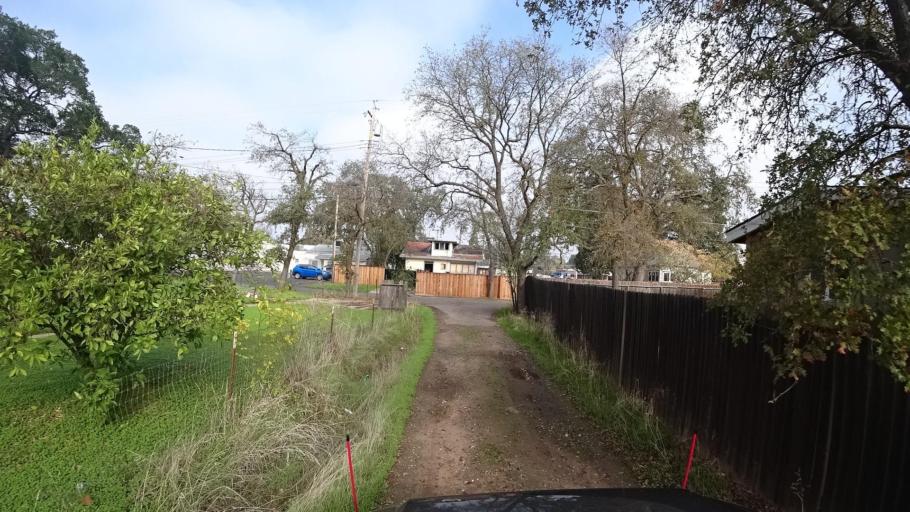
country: US
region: California
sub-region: Sacramento County
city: Elk Grove
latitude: 38.4082
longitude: -121.3670
